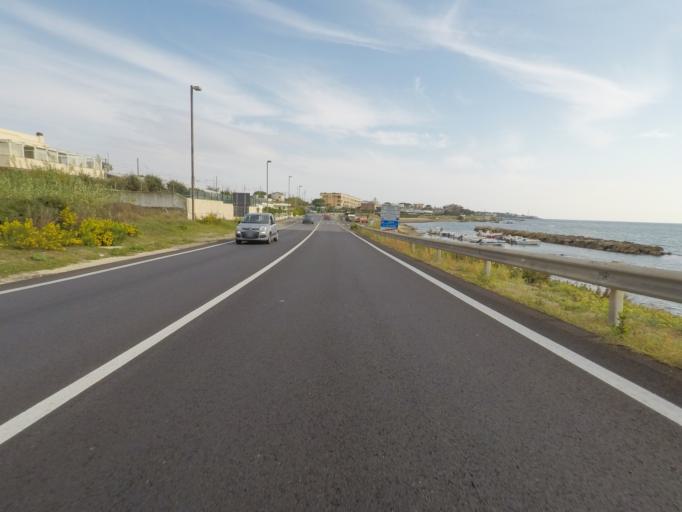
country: IT
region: Latium
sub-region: Citta metropolitana di Roma Capitale
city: Santa Marinella
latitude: 42.0454
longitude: 11.8252
